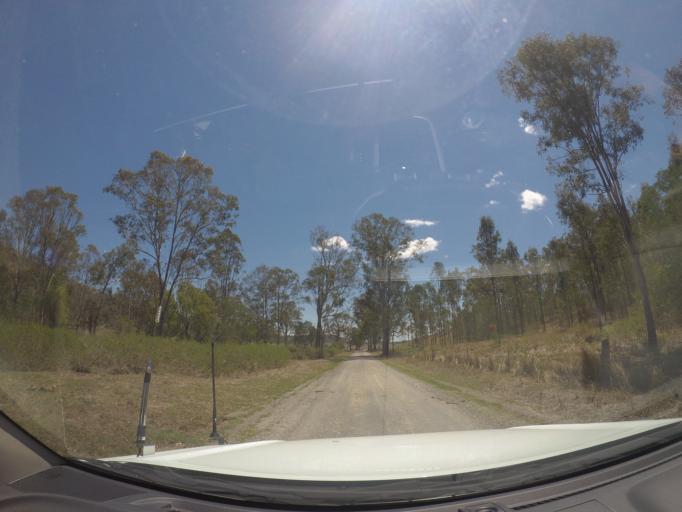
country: AU
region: Queensland
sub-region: Ipswich
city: Redbank Plains
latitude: -27.7542
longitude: 152.8349
